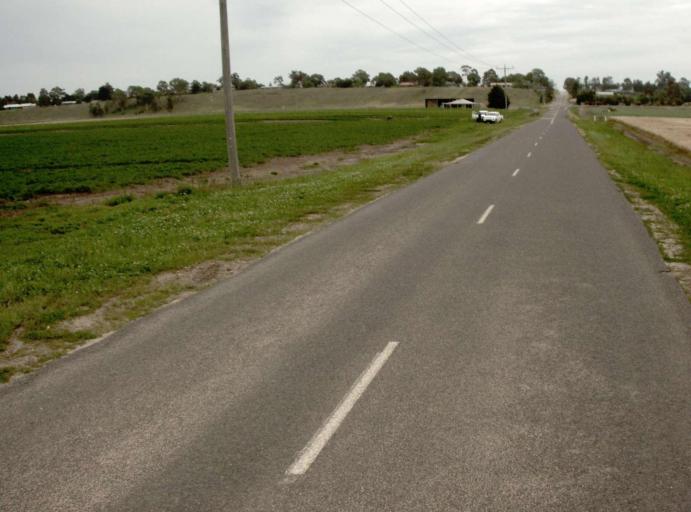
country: AU
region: Victoria
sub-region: East Gippsland
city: Bairnsdale
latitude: -37.7939
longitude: 147.4409
